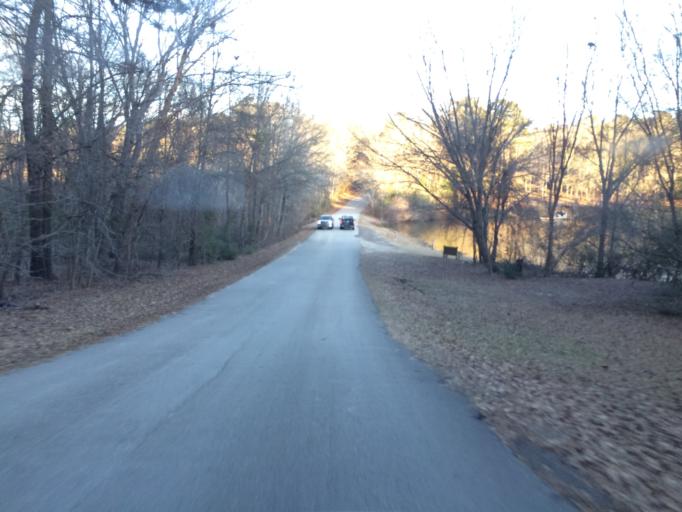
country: US
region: Texas
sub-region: Wood County
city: Hawkins
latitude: 32.7253
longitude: -95.1865
